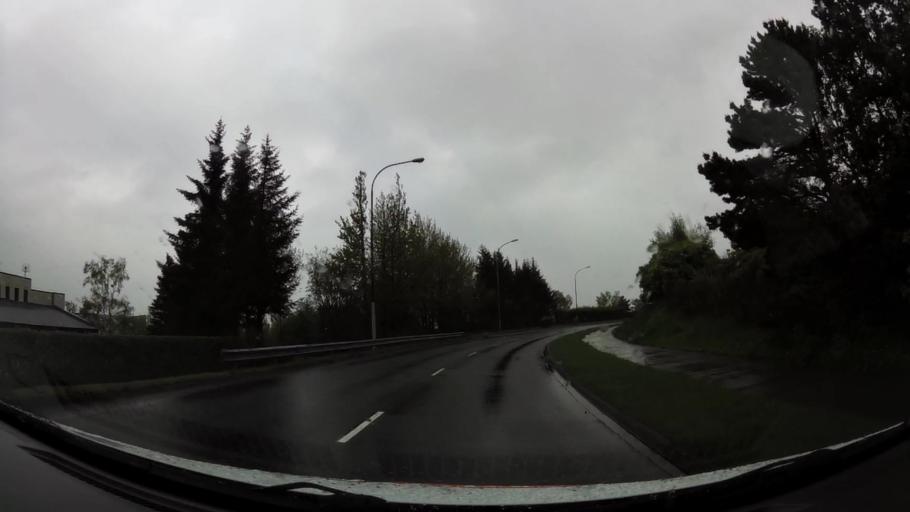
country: IS
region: Capital Region
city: Reykjavik
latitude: 64.1015
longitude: -21.8424
